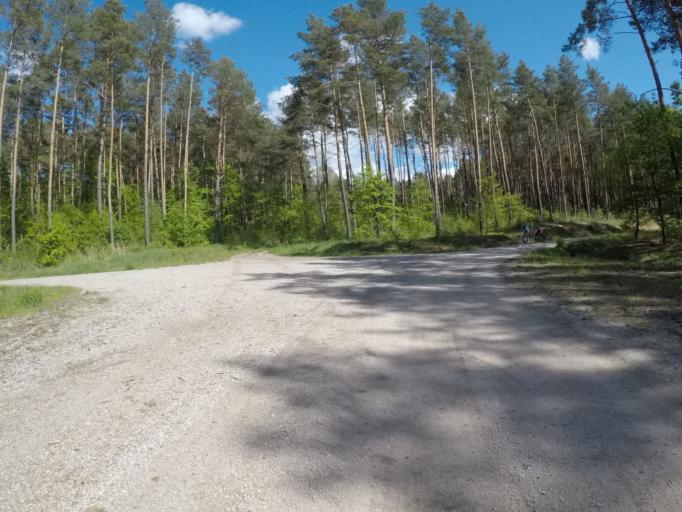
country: PL
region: Swietokrzyskie
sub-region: Powiat kielecki
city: Miedziana Gora
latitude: 50.9027
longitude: 20.5303
